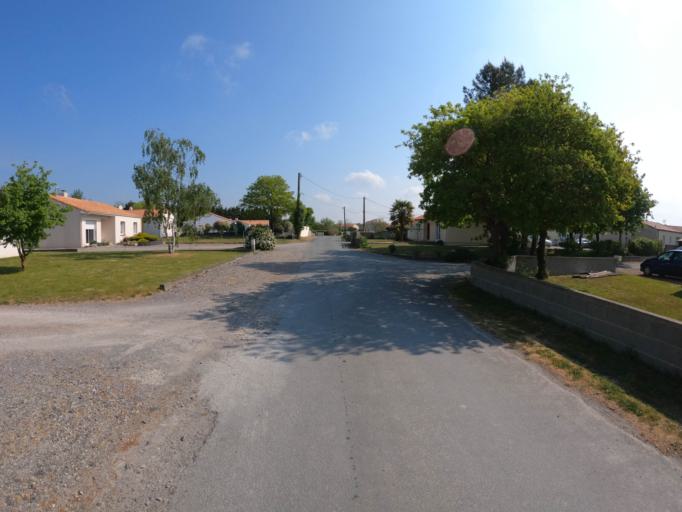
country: FR
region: Pays de la Loire
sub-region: Departement de la Vendee
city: Treize-Septiers
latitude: 46.9997
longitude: -1.2402
